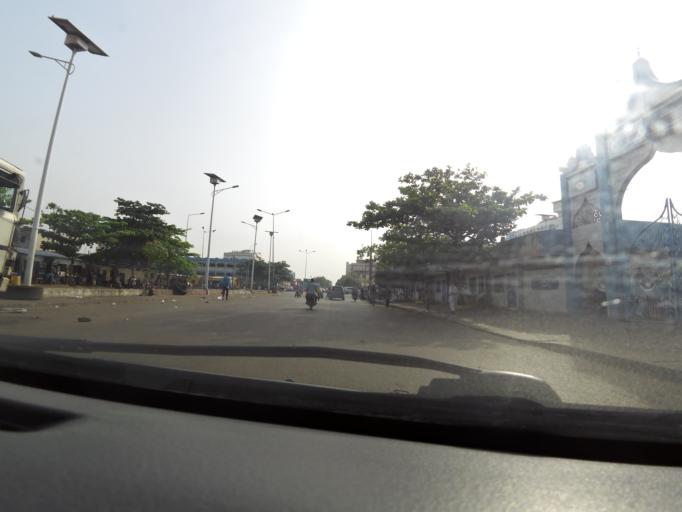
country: BJ
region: Littoral
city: Cotonou
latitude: 6.3570
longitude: 2.4256
